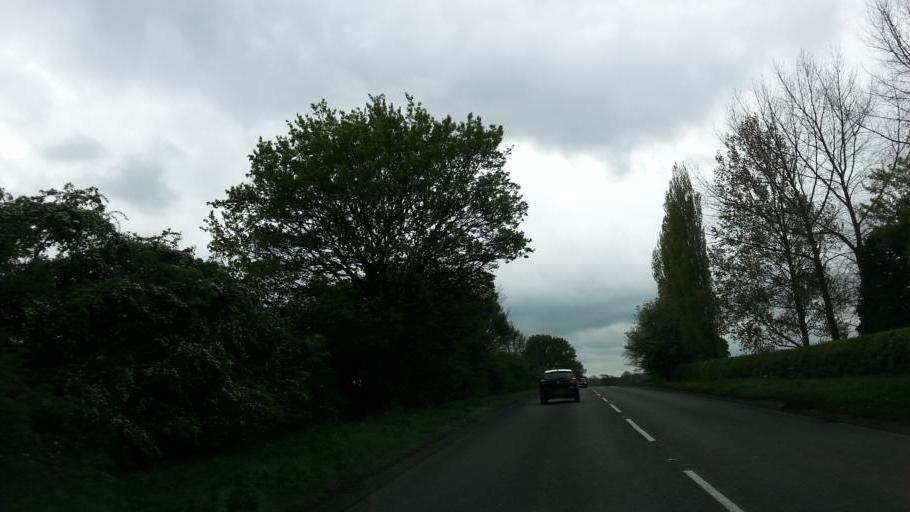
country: GB
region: England
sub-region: Leicestershire
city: Lutterworth
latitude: 52.4446
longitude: -1.1964
